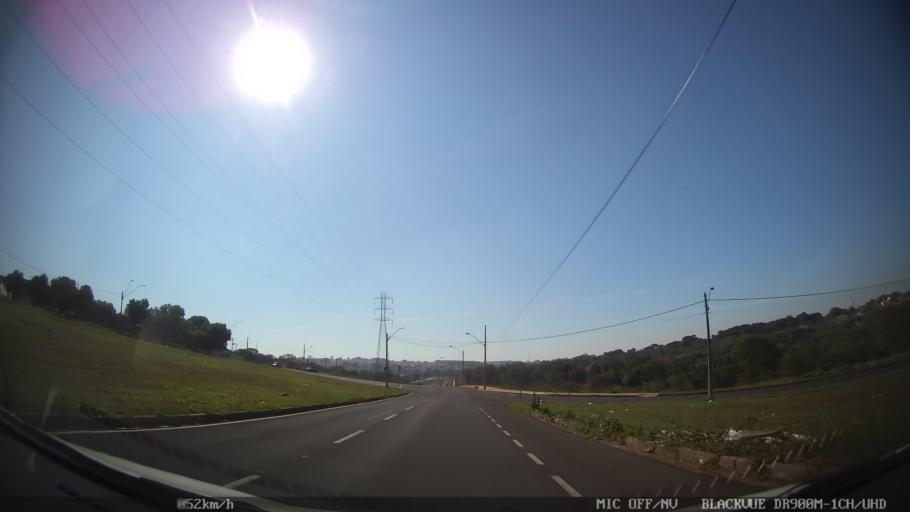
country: BR
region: Sao Paulo
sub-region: Sao Jose Do Rio Preto
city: Sao Jose do Rio Preto
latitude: -20.7640
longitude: -49.3778
